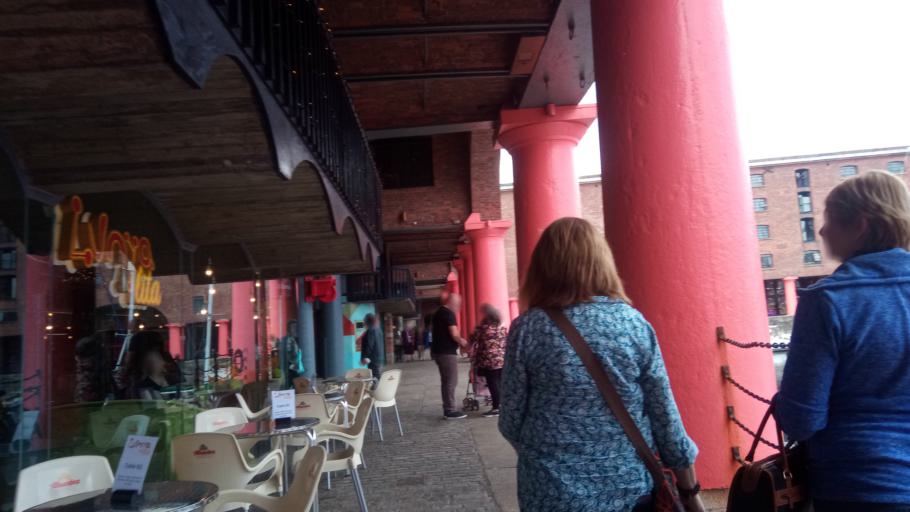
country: GB
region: England
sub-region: Liverpool
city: Liverpool
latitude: 53.3999
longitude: -2.9919
